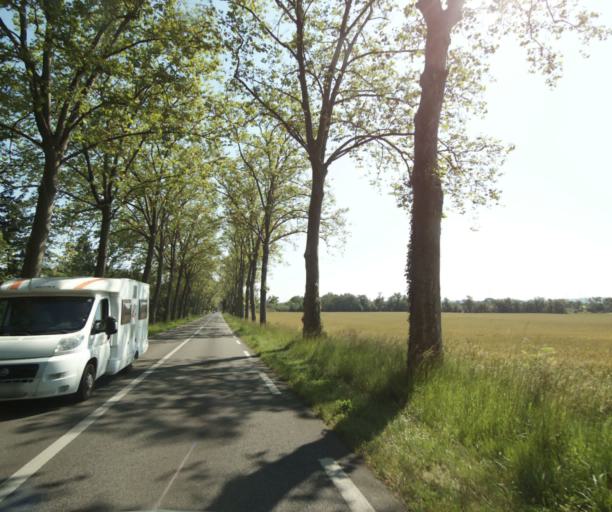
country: FR
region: Midi-Pyrenees
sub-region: Departement du Tarn-et-Garonne
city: Montbeton
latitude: 43.9871
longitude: 1.3048
